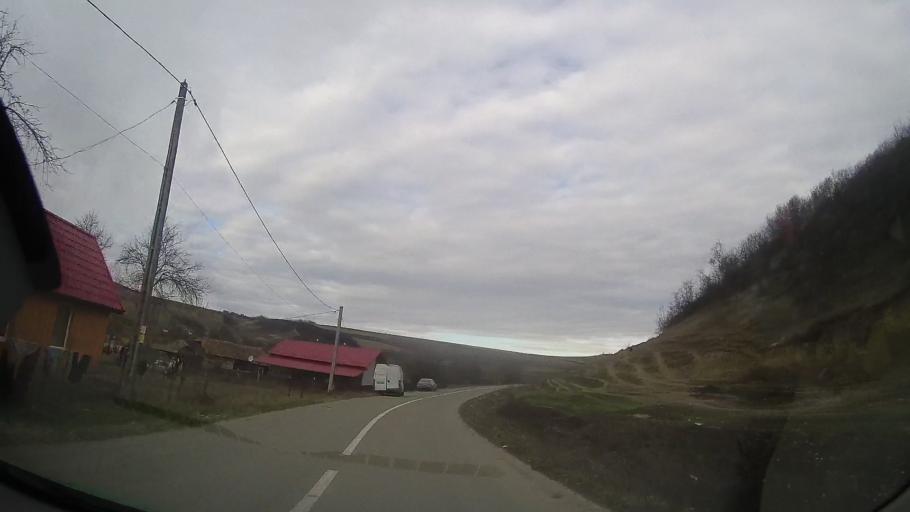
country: RO
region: Bistrita-Nasaud
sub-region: Comuna Silvasu de Campie
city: Silvasu de Campie
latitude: 46.7853
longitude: 24.2868
